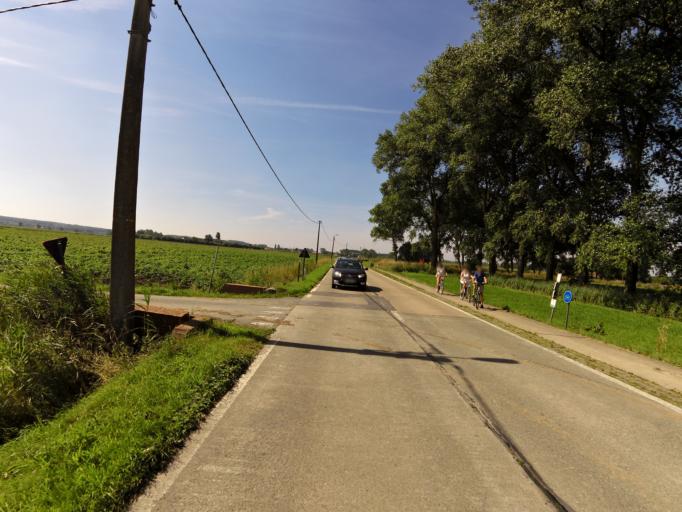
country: BE
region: Flanders
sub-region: Provincie West-Vlaanderen
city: Damme
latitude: 51.2579
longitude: 3.2605
